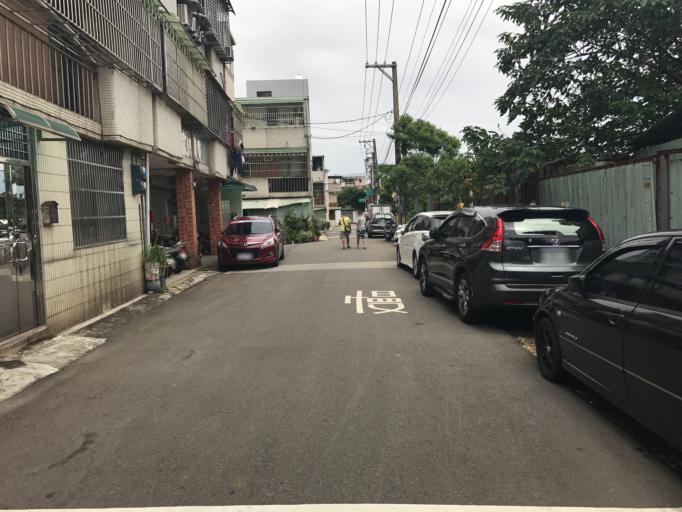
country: TW
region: Taiwan
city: Taoyuan City
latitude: 24.9489
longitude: 121.2481
